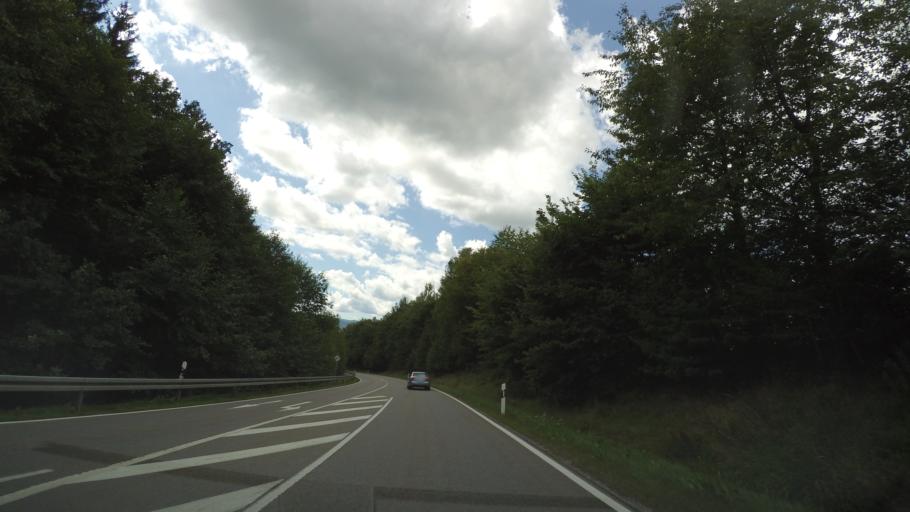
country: DE
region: Bavaria
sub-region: Lower Bavaria
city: Bobrach
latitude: 49.0549
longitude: 13.0413
